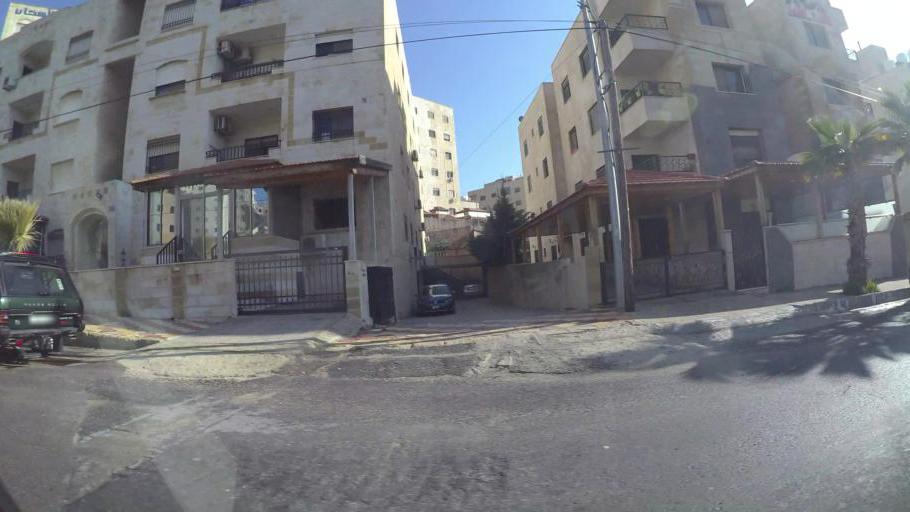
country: JO
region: Amman
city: Al Jubayhah
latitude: 32.0014
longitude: 35.8557
